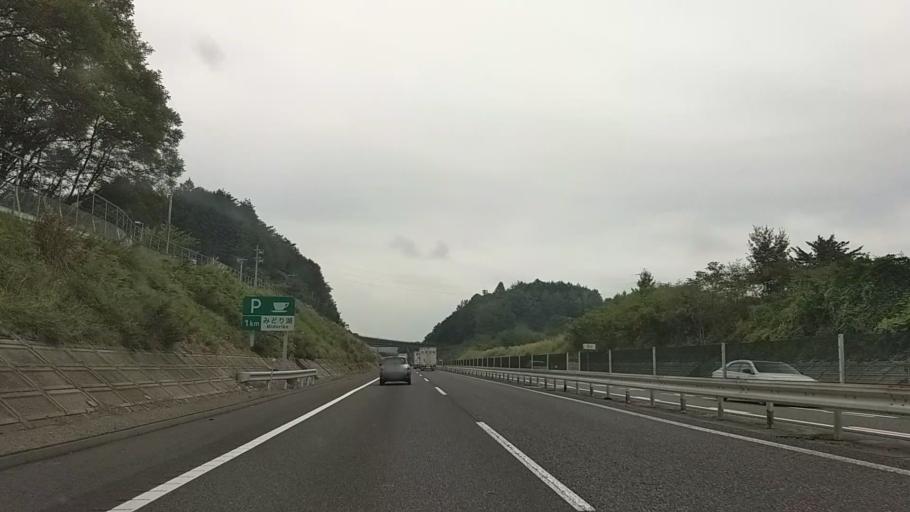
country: JP
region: Nagano
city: Shiojiri
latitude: 36.1083
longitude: 137.9883
